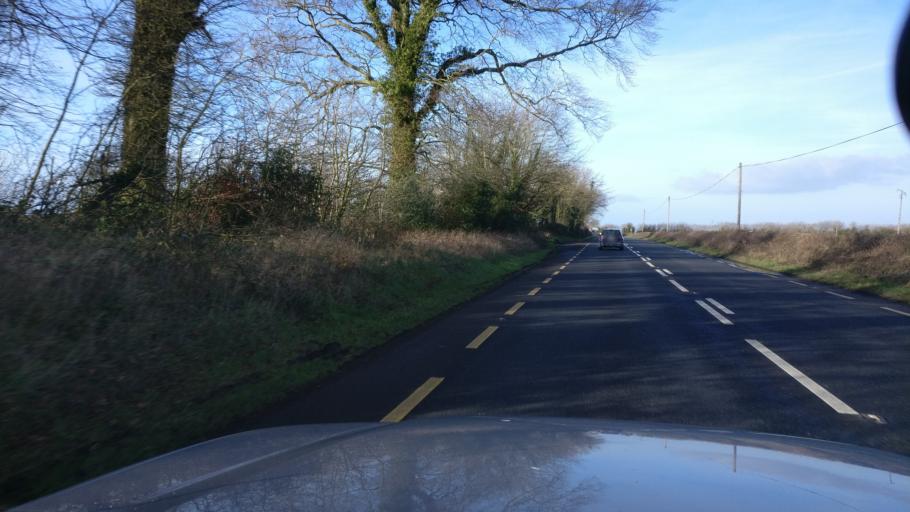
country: IE
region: Leinster
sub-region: Uibh Fhaili
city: Tullamore
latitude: 53.2031
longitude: -7.4332
